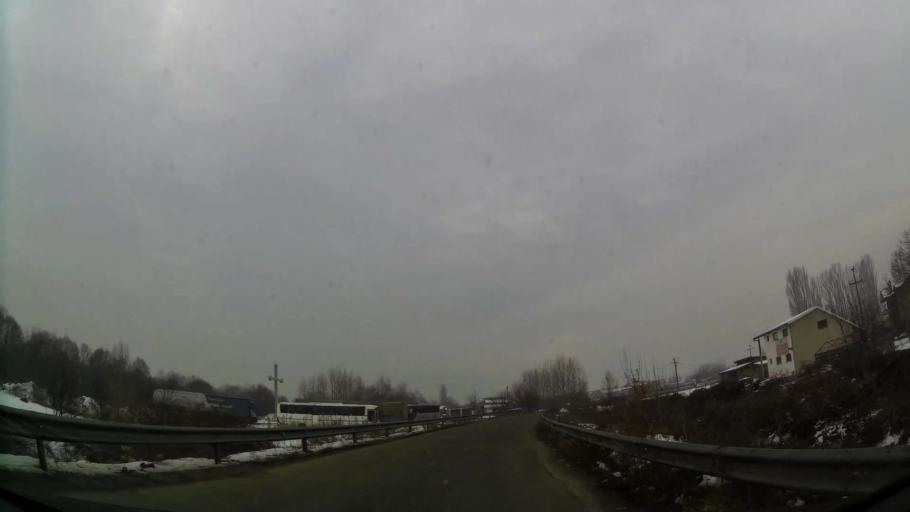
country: MK
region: Cucer-Sandevo
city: Chucher - Sandevo
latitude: 42.0471
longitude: 21.3664
